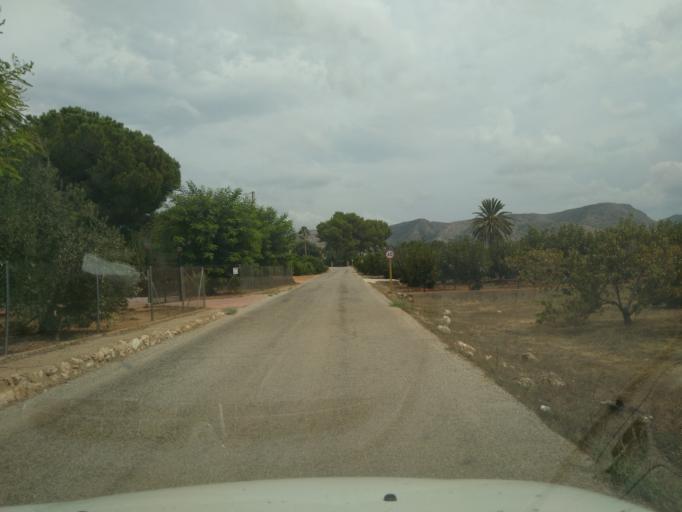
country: ES
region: Valencia
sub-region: Provincia de Valencia
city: Rafelguaraf
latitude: 39.0746
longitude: -0.4270
